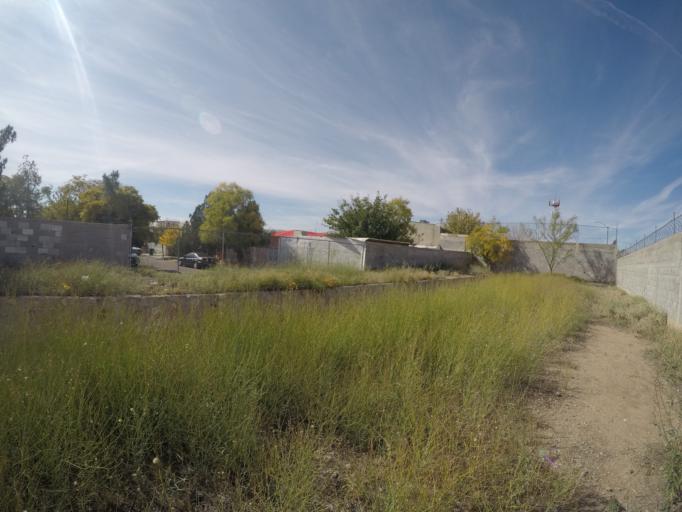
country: MX
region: Chihuahua
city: Ciudad Juarez
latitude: 31.7359
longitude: -106.4549
